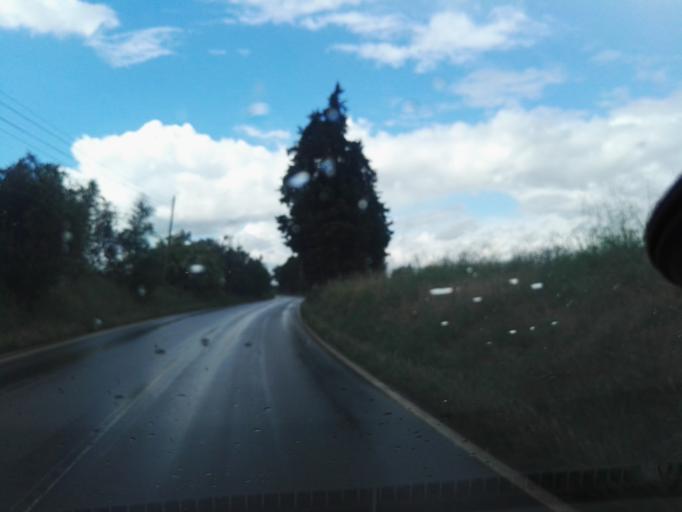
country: PT
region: Santarem
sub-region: Golega
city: Golega
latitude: 39.4208
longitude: -8.4963
